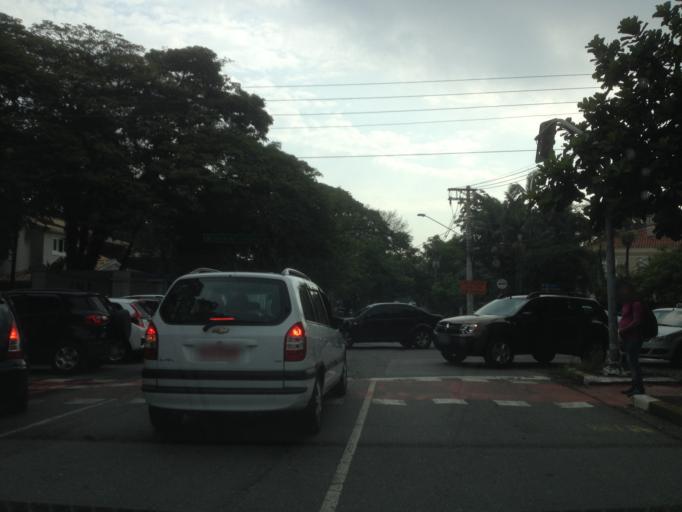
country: BR
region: Sao Paulo
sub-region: Sao Paulo
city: Sao Paulo
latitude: -23.5712
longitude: -46.6657
